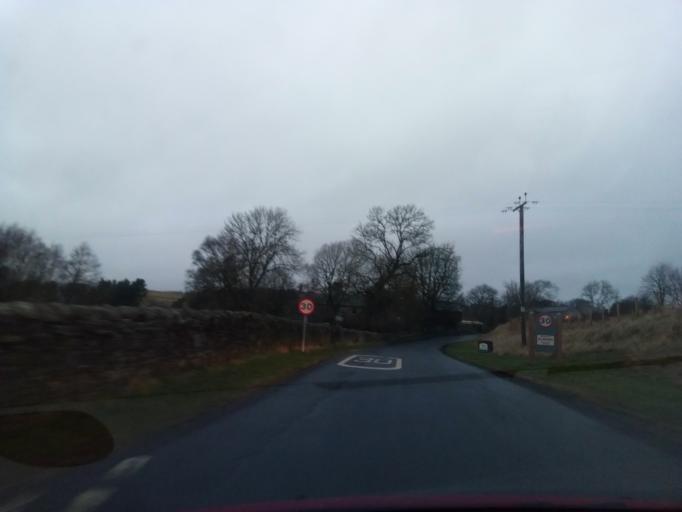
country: GB
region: England
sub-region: Northumberland
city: Otterburn
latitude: 55.2304
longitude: -2.1036
